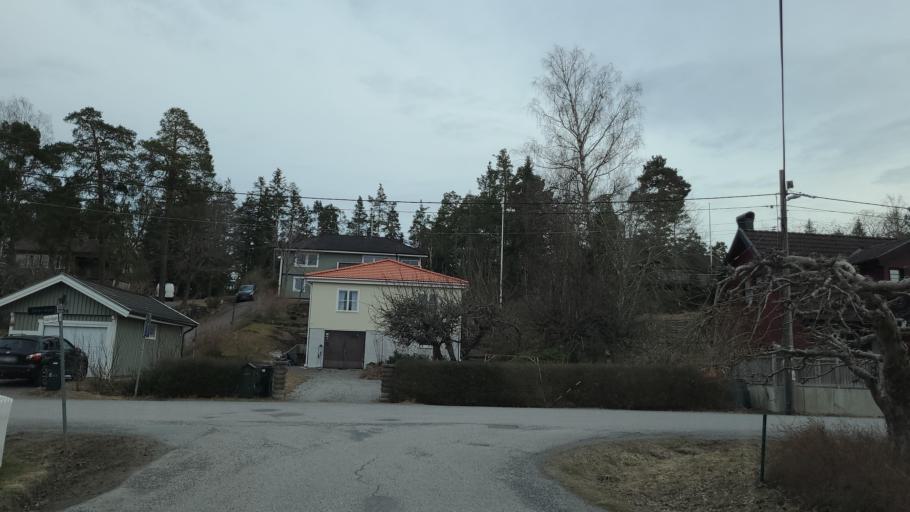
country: SE
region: Stockholm
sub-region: Nacka Kommun
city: Boo
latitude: 59.3182
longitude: 18.2661
